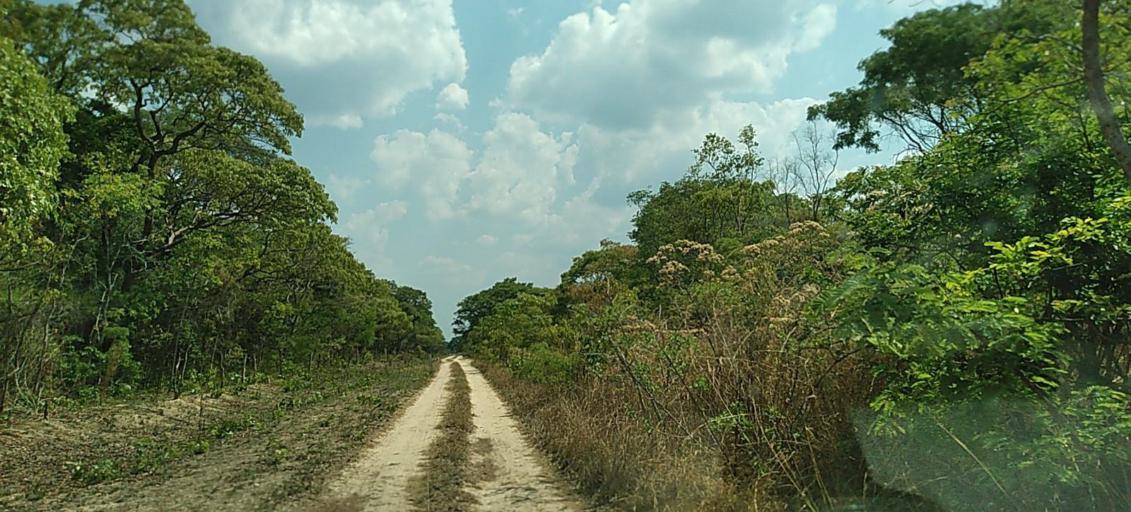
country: ZM
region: Copperbelt
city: Mpongwe
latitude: -13.8414
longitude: 27.9355
